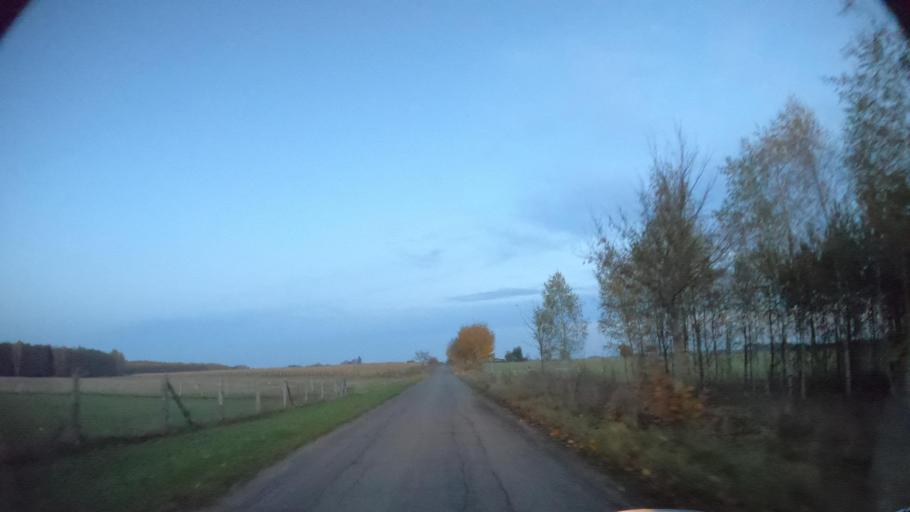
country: PL
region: Greater Poland Voivodeship
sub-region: Powiat zlotowski
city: Sypniewo
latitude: 53.4265
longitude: 16.6094
